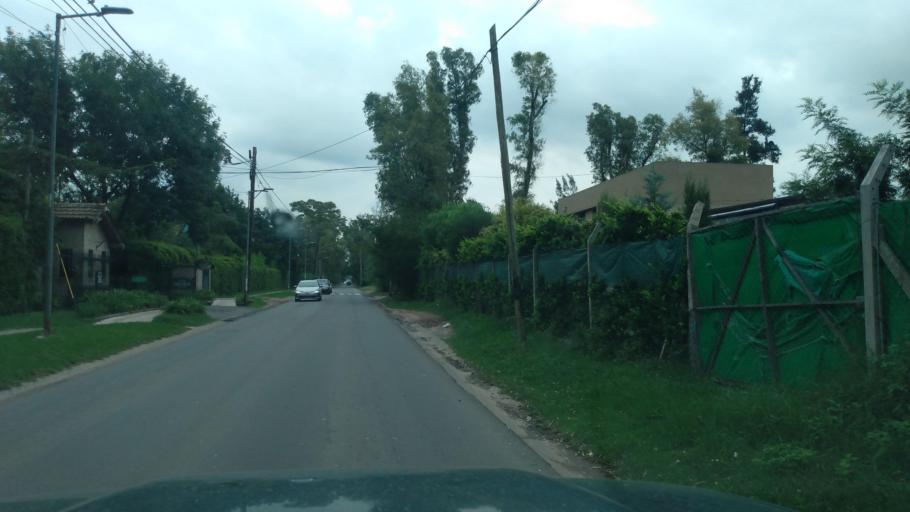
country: AR
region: Buenos Aires
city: Hurlingham
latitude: -34.5762
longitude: -58.7023
